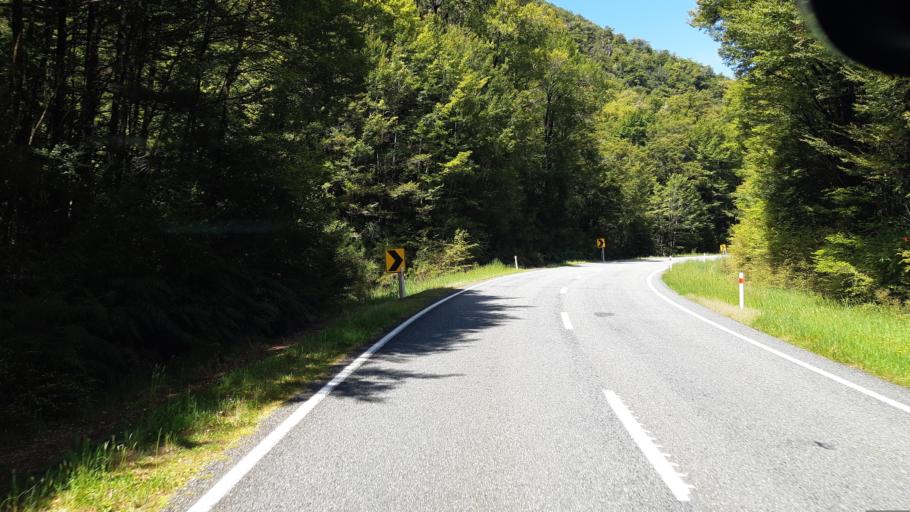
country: NZ
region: West Coast
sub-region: Buller District
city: Westport
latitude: -42.2852
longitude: 172.0038
